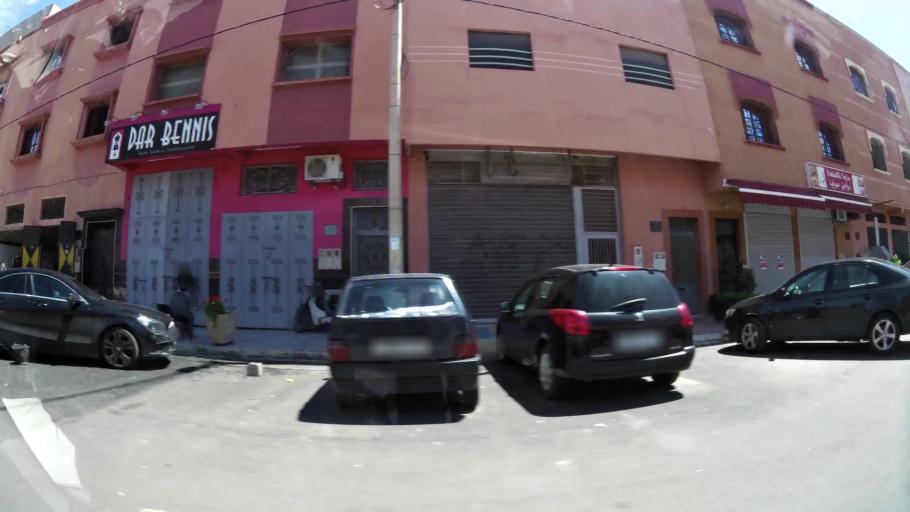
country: MA
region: Marrakech-Tensift-Al Haouz
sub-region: Marrakech
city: Marrakesh
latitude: 31.6416
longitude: -8.0475
